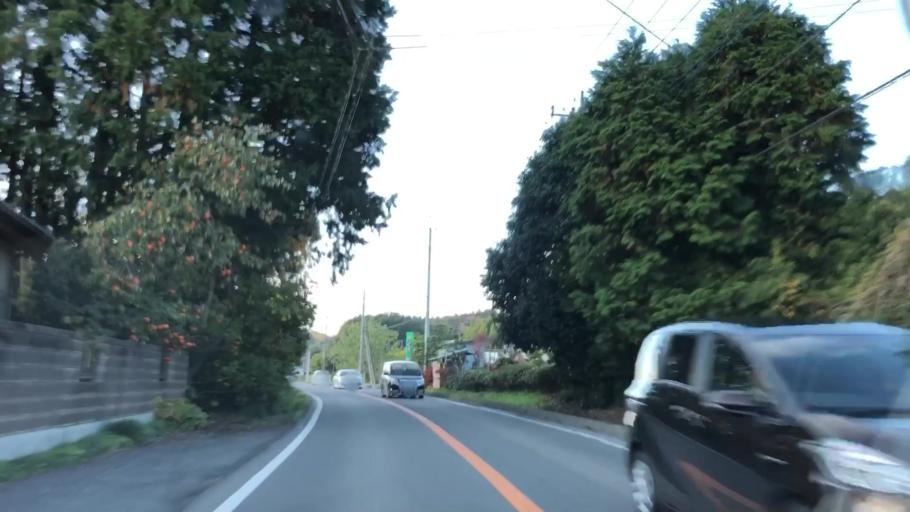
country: JP
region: Ibaraki
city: Kasama
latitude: 36.4661
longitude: 140.3192
